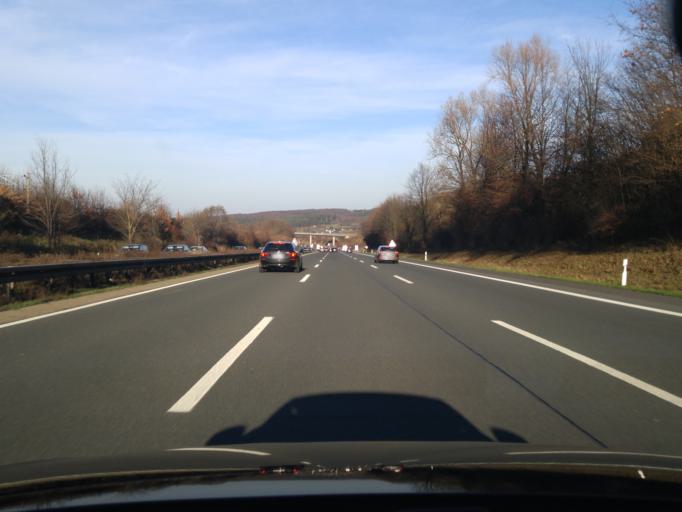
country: DE
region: North Rhine-Westphalia
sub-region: Regierungsbezirk Koln
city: Stossdorf
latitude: 50.7344
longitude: 7.2387
